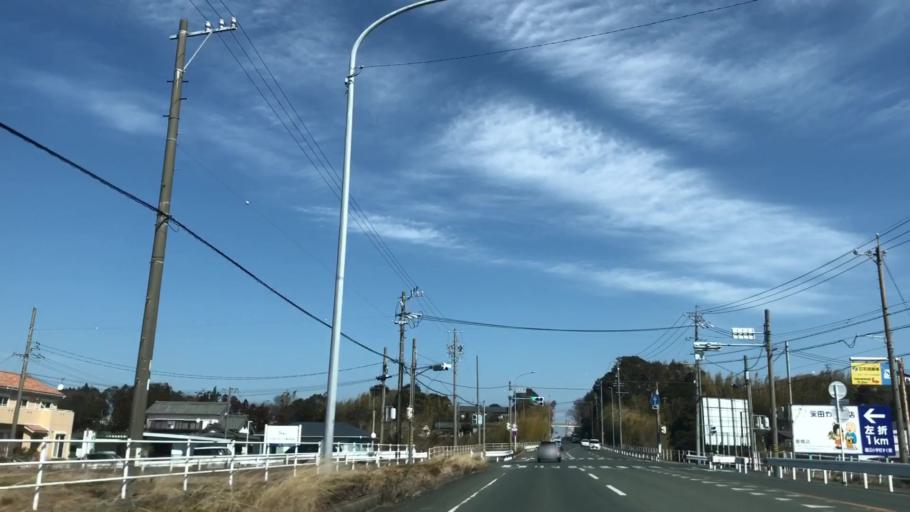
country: JP
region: Aichi
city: Toyohashi
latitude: 34.7206
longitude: 137.3711
